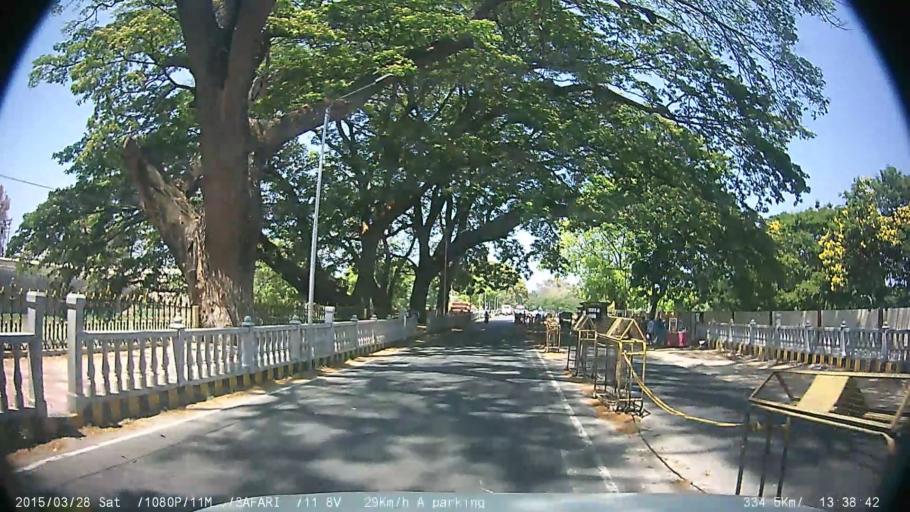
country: IN
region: Karnataka
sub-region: Mysore
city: Mysore
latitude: 12.3033
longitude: 76.6581
